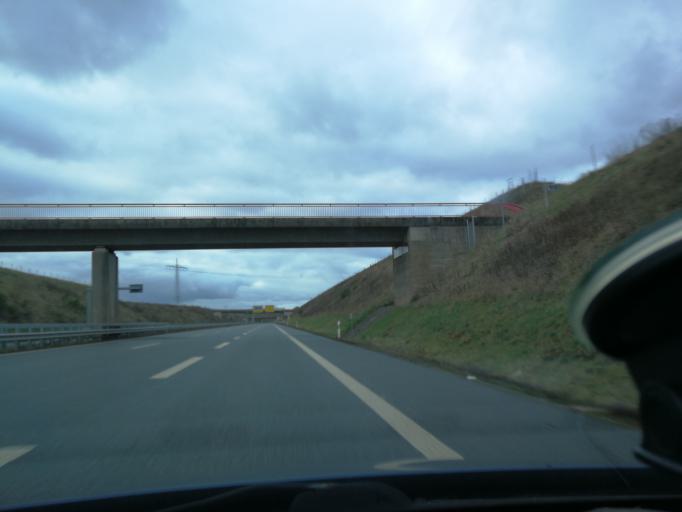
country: DE
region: Rheinland-Pfalz
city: Altrich
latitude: 49.9535
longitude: 6.9285
